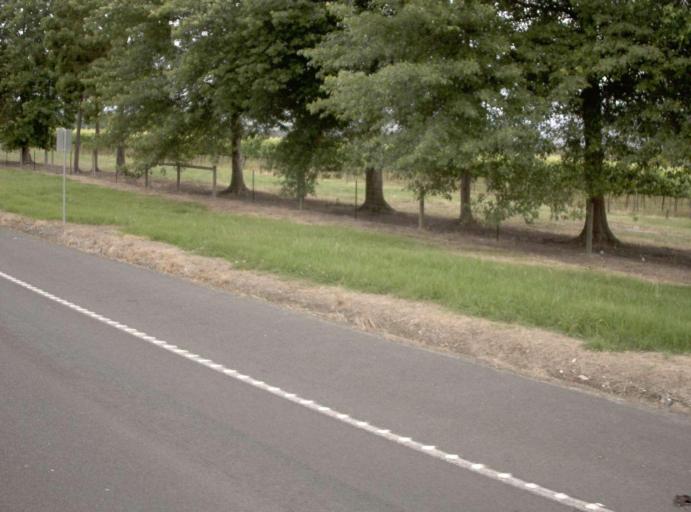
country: AU
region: Victoria
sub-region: Yarra Ranges
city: Healesville
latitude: -37.6764
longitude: 145.5060
